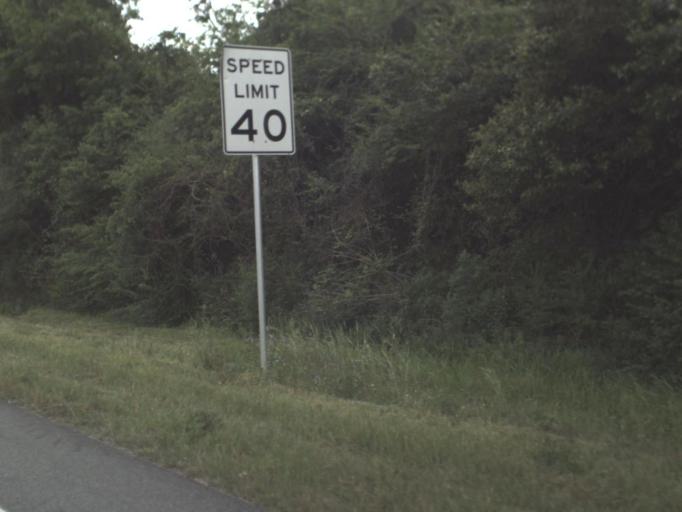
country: US
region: Florida
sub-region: Escambia County
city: Cantonment
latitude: 30.6164
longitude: -87.3238
